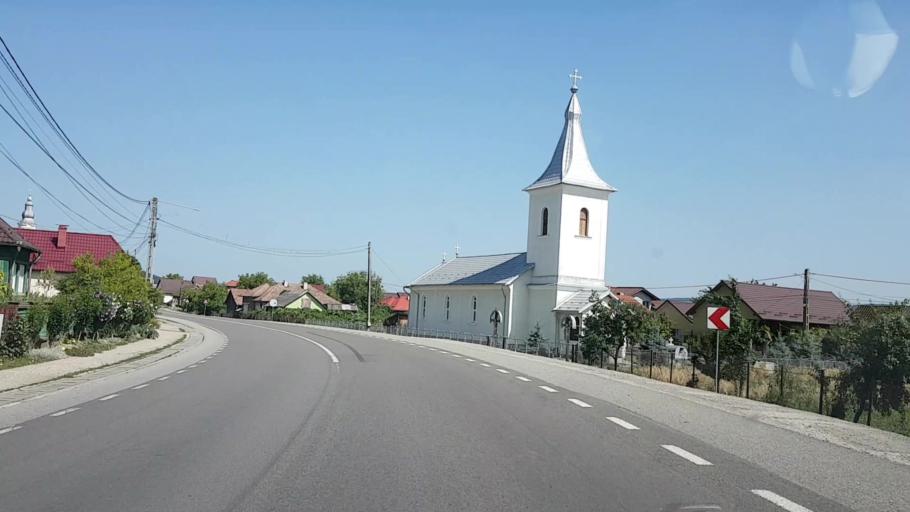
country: RO
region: Bistrita-Nasaud
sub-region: Comuna Uriu
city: Cristestii Ciceului
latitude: 47.1937
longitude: 24.0865
